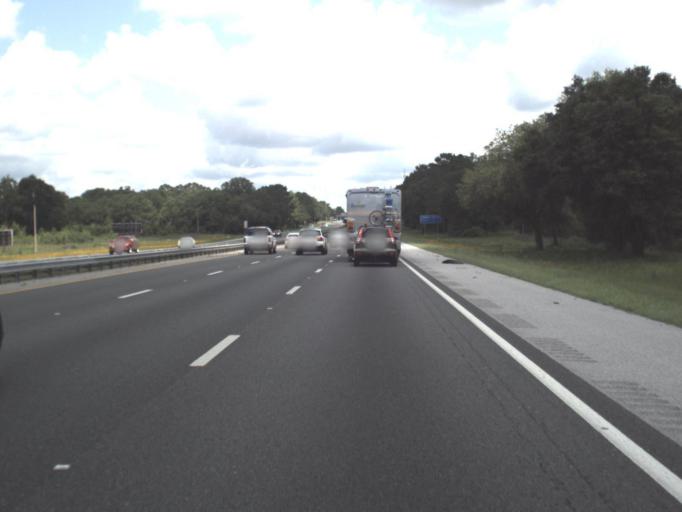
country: US
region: Florida
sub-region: Suwannee County
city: Wellborn
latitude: 30.3086
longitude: -82.7976
